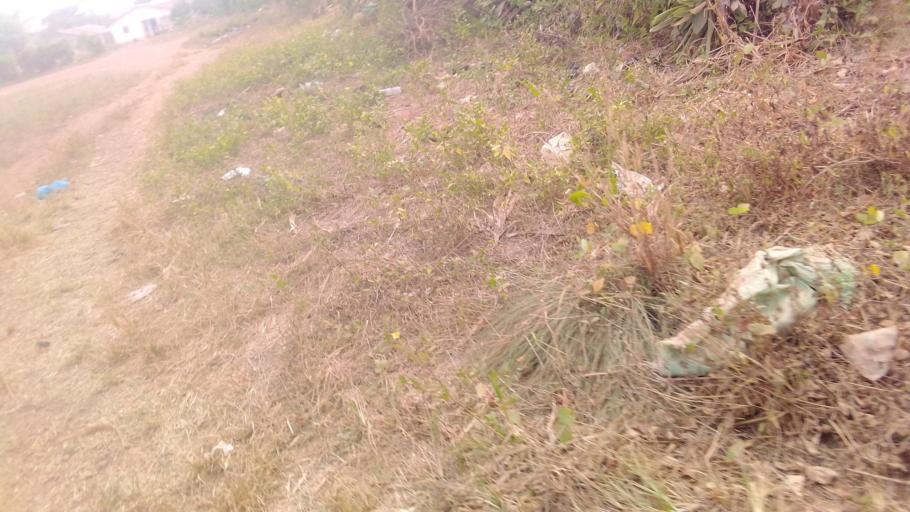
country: SL
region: Southern Province
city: Mogbwemo
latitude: 7.7776
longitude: -12.2947
